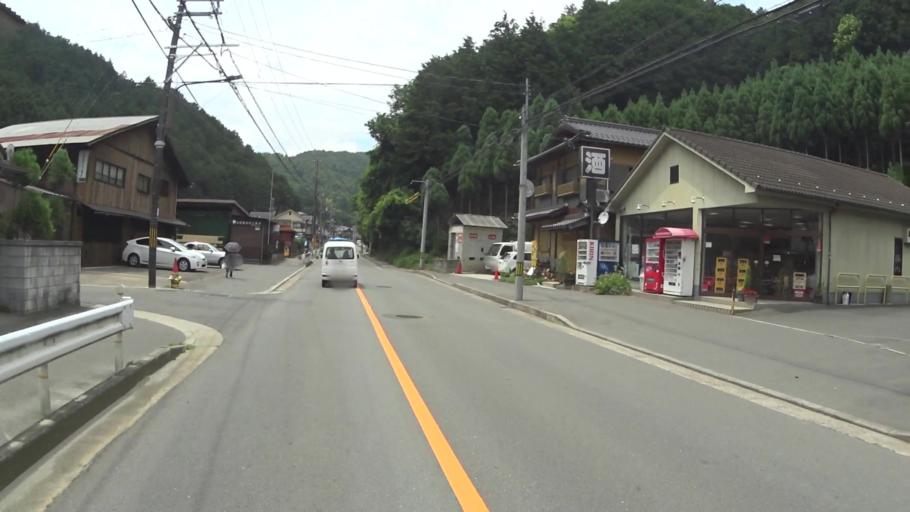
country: JP
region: Kyoto
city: Kyoto
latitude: 35.0375
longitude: 135.6910
